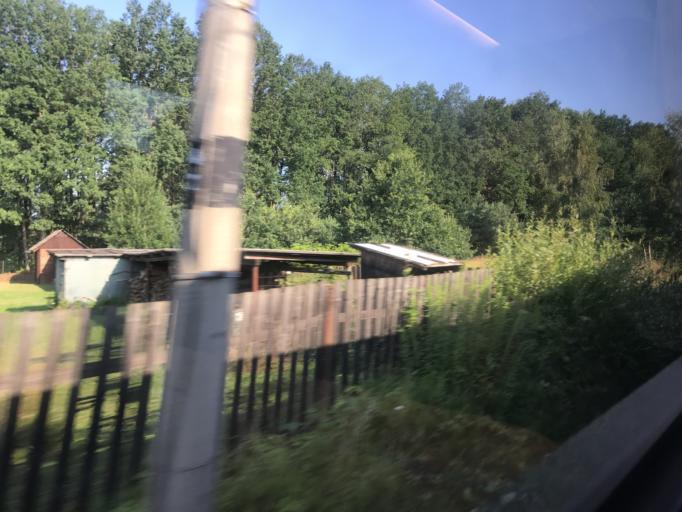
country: CZ
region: Jihocesky
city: Sobeslav
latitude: 49.2711
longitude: 14.7045
